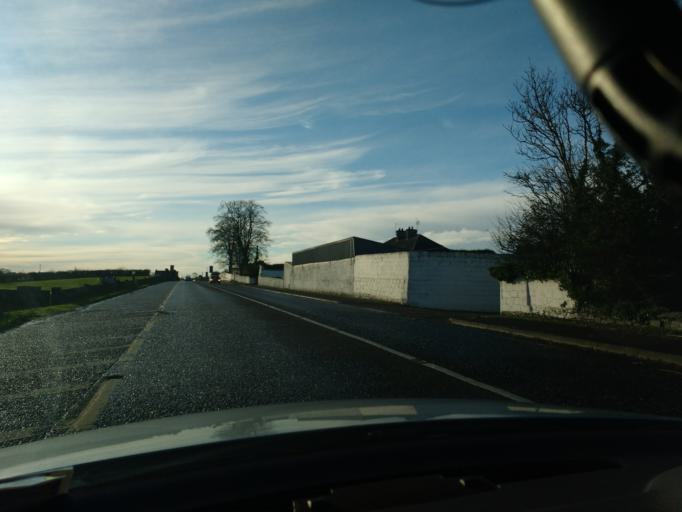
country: IE
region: Munster
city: Thurles
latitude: 52.6374
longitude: -7.7416
